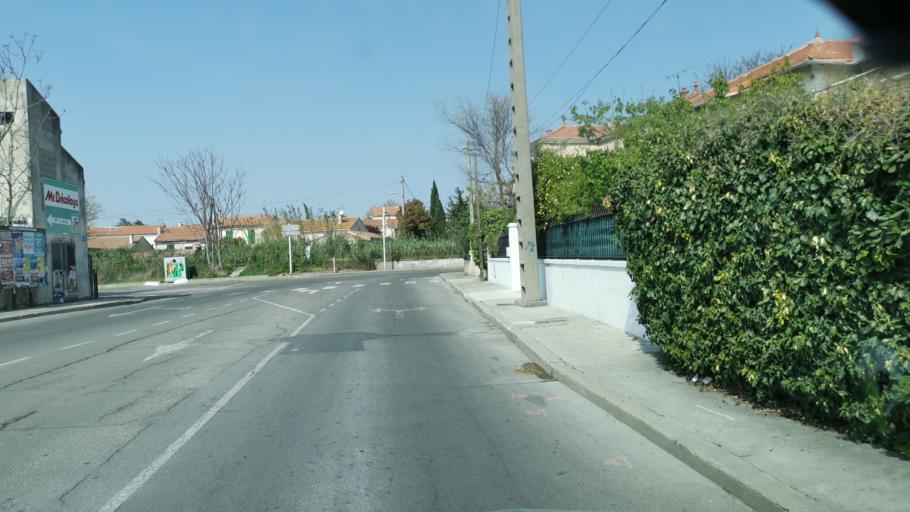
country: FR
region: Provence-Alpes-Cote d'Azur
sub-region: Departement des Bouches-du-Rhone
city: Arles
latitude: 43.6723
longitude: 4.6330
